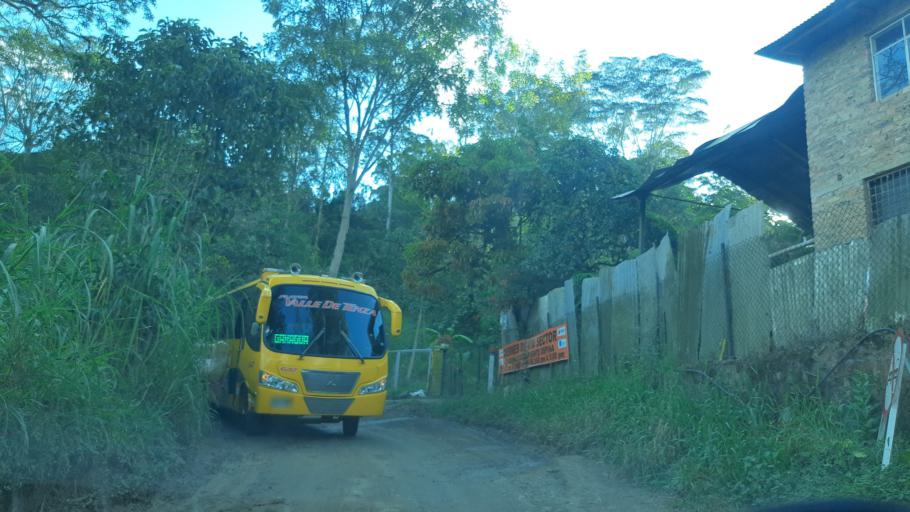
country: CO
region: Boyaca
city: Garagoa
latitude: 5.0848
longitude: -73.3880
